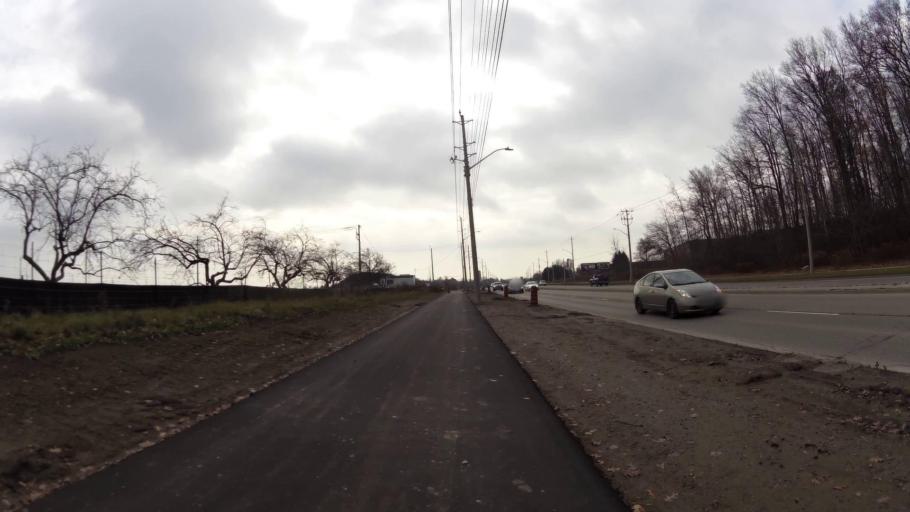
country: CA
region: Ontario
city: Kitchener
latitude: 43.4065
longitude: -80.4583
